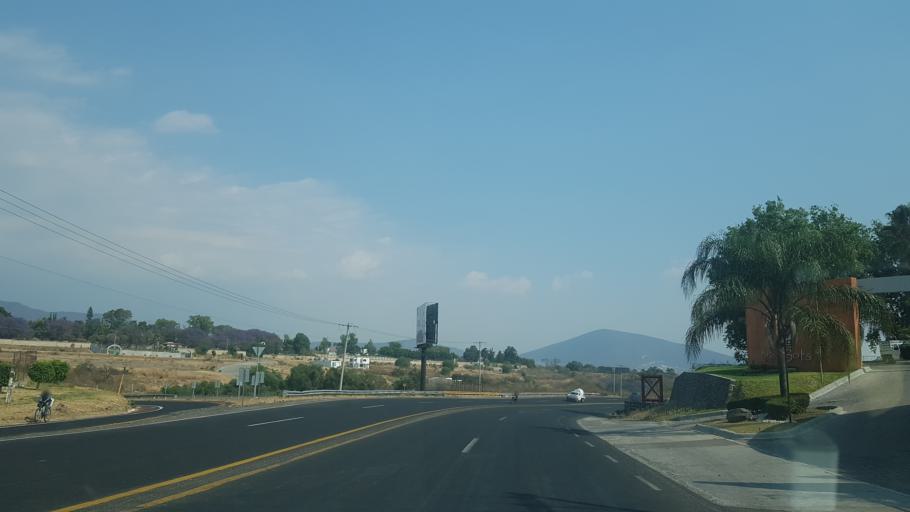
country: MX
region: Puebla
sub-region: Atlixco
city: San Agustin Huixaxtla
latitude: 18.9219
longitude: -98.4094
